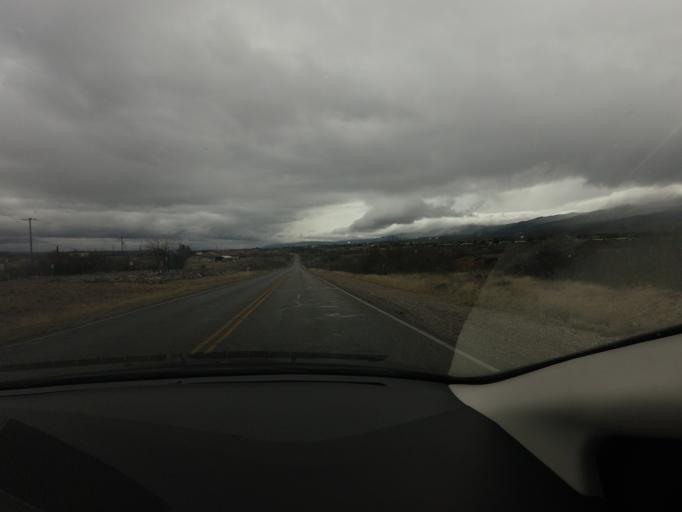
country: US
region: Arizona
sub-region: Yavapai County
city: Clarkdale
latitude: 34.7593
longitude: -112.0383
